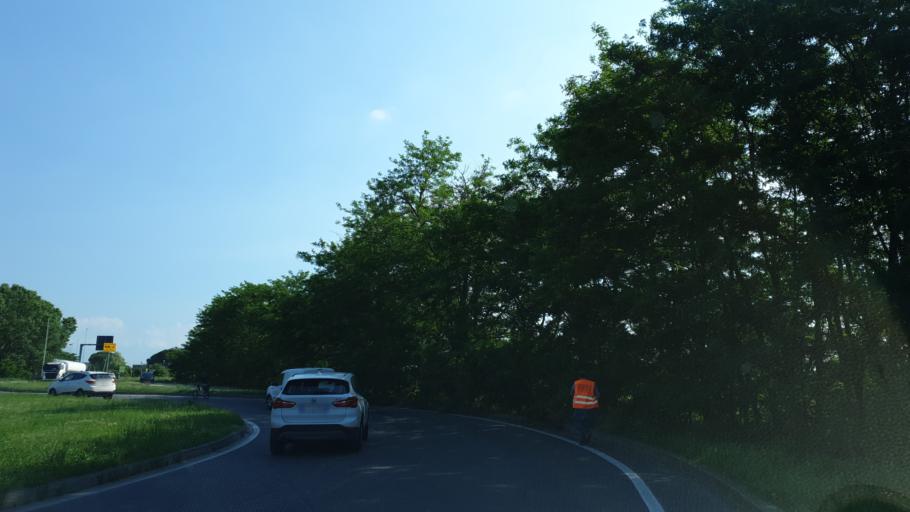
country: IT
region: Emilia-Romagna
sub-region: Provincia di Ravenna
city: Ravenna
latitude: 44.4428
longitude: 12.2109
